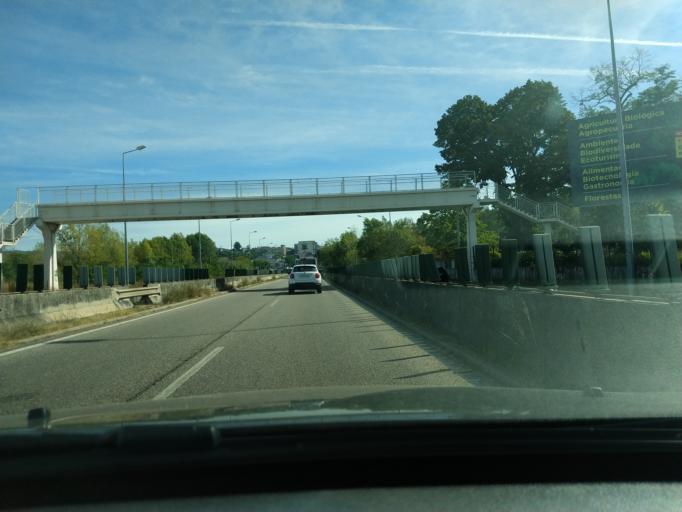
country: PT
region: Coimbra
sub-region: Coimbra
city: Coimbra
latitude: 40.2143
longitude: -8.4518
